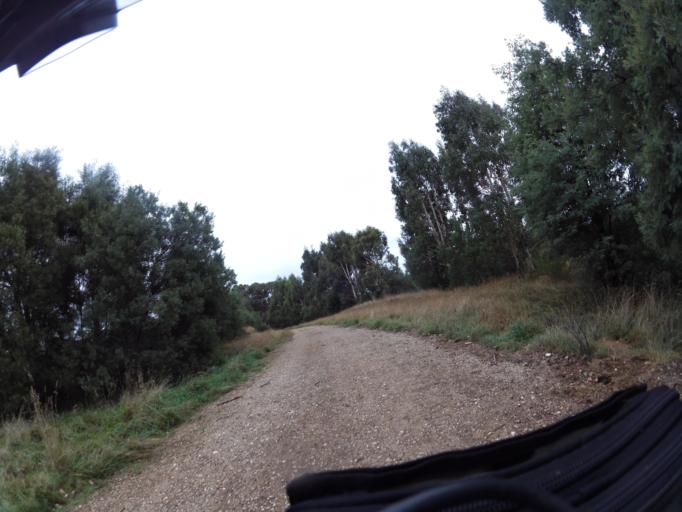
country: AU
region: New South Wales
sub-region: Greater Hume Shire
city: Holbrook
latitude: -36.1534
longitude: 147.4870
